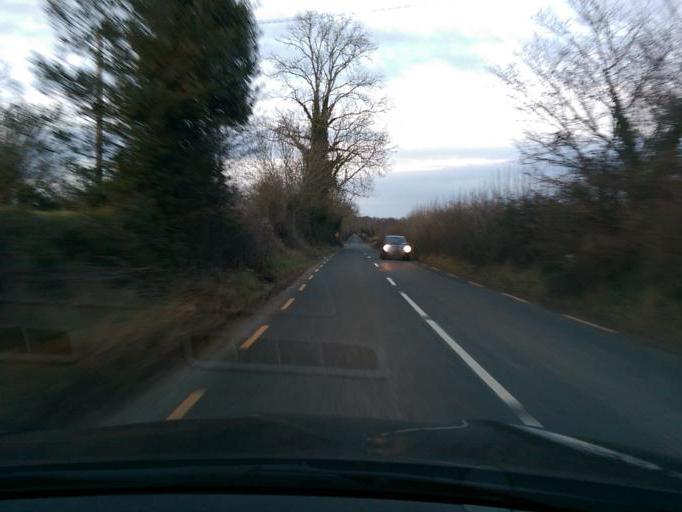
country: IE
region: Leinster
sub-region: Uibh Fhaili
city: Banagher
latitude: 53.0809
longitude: -8.0678
